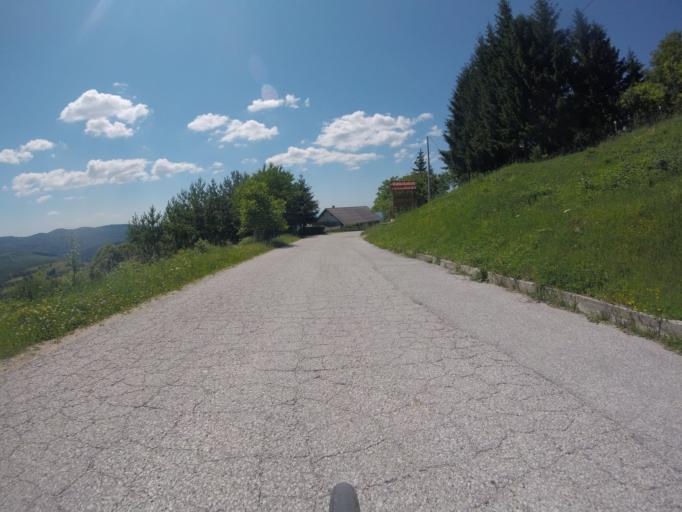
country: SI
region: Kostanjevica na Krki
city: Kostanjevica na Krki
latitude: 45.7739
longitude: 15.4702
